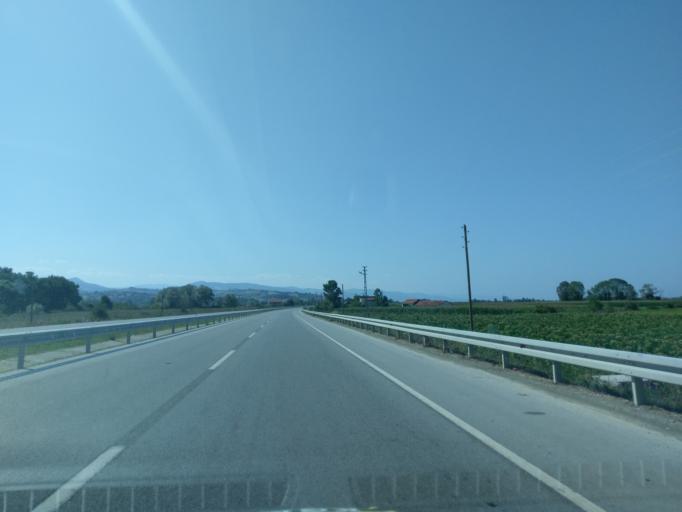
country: TR
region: Samsun
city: Alacam
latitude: 41.6084
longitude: 35.6697
